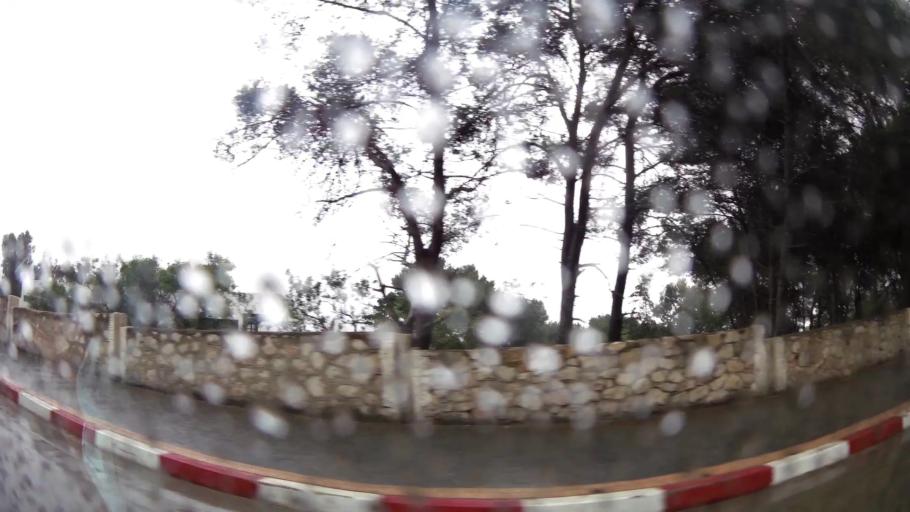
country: MA
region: Taza-Al Hoceima-Taounate
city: Al Hoceima
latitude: 35.2474
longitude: -3.9392
